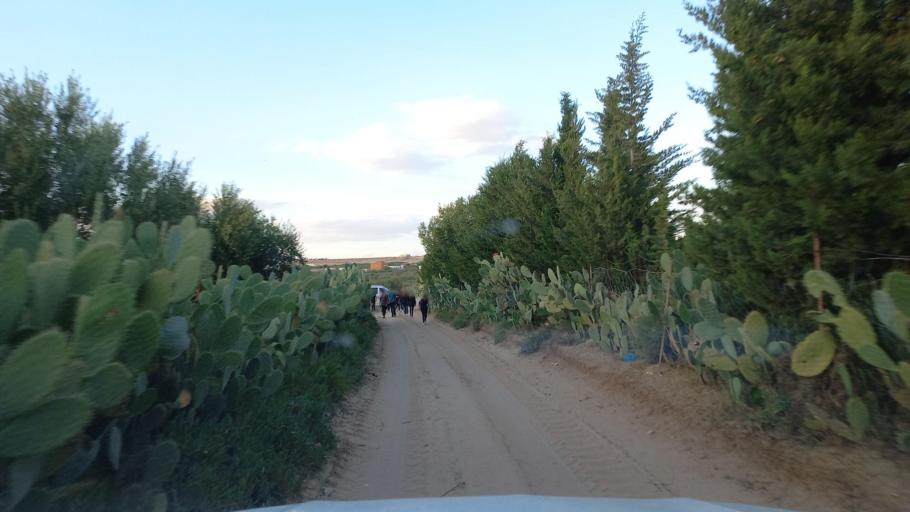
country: TN
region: Al Qasrayn
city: Sbiba
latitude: 35.3791
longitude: 9.0566
